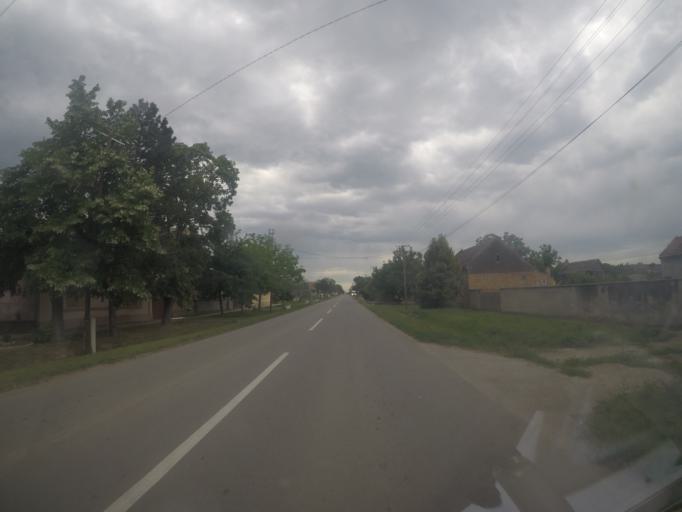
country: RS
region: Autonomna Pokrajina Vojvodina
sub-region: Juznobanatski Okrug
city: Opovo
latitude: 45.0459
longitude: 20.4362
